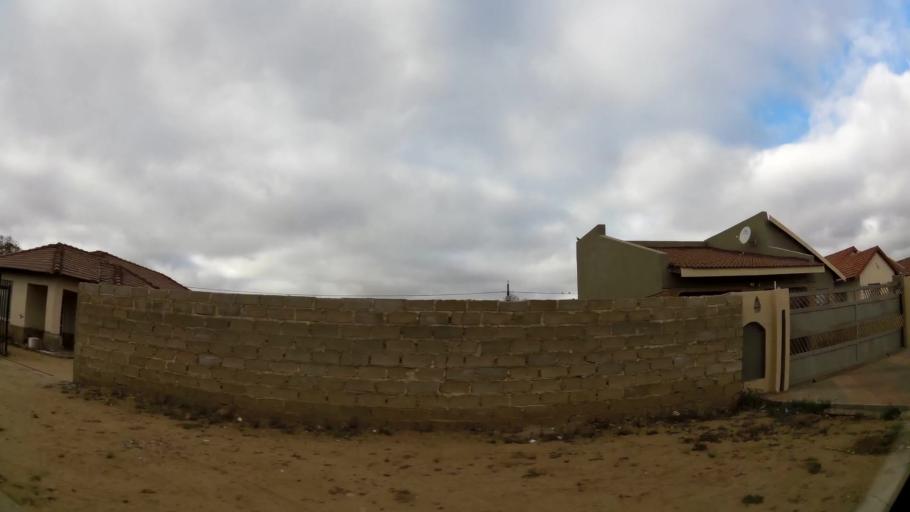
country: ZA
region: Limpopo
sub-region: Capricorn District Municipality
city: Polokwane
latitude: -23.9257
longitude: 29.4472
